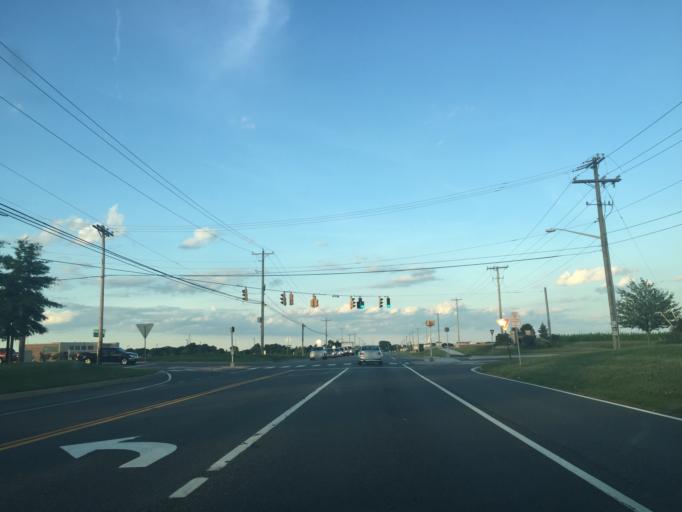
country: US
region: Delaware
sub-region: New Castle County
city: Middletown
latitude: 39.4525
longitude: -75.6872
